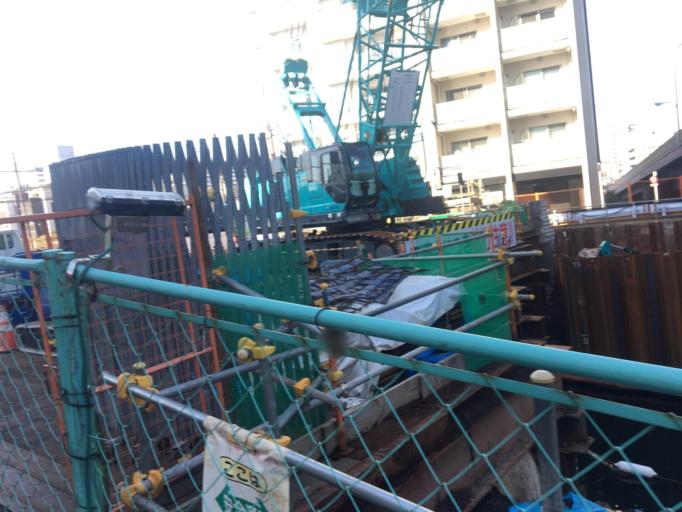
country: JP
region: Tokyo
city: Urayasu
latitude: 35.7028
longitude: 139.8337
